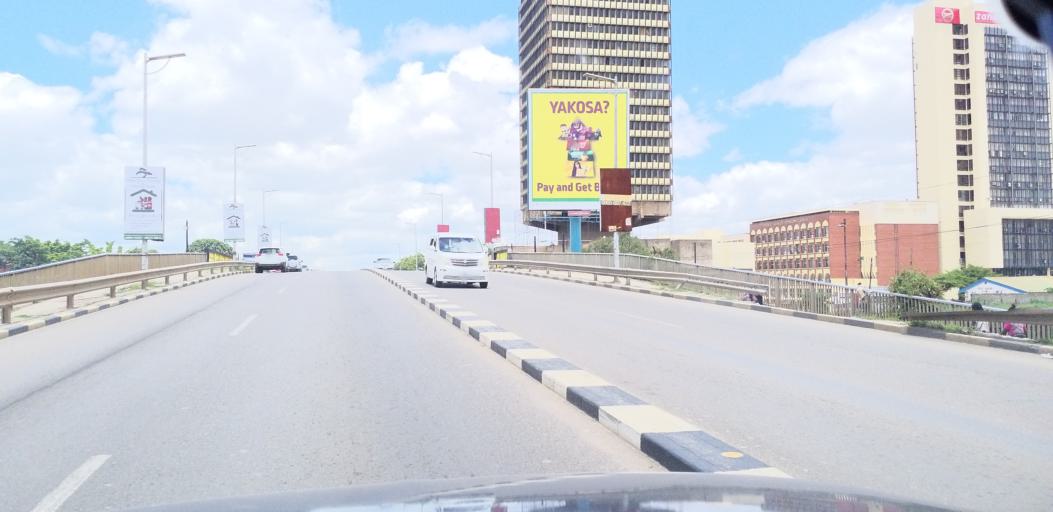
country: ZM
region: Lusaka
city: Lusaka
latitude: -15.4246
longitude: 28.2854
